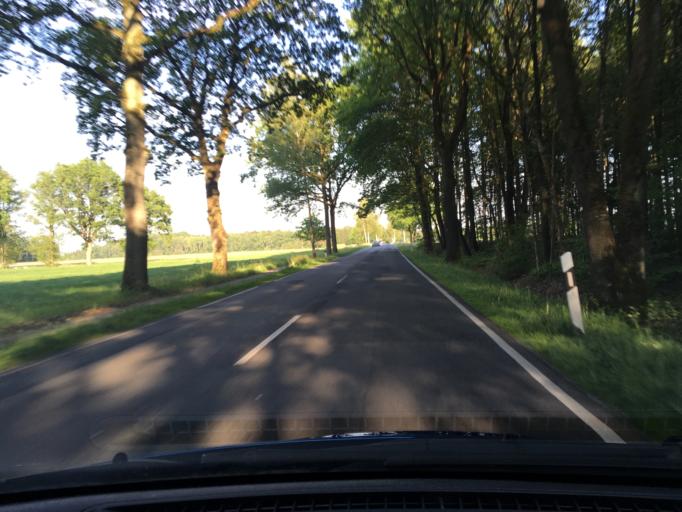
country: DE
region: Lower Saxony
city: Otter
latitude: 53.2549
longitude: 9.7541
